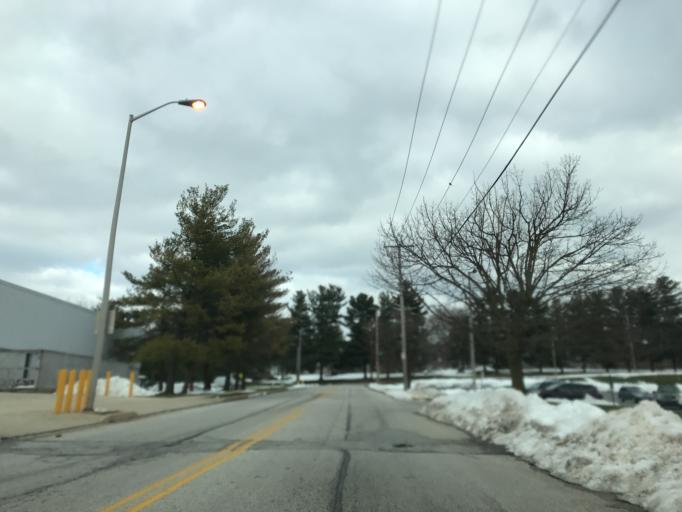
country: US
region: Pennsylvania
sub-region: York County
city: North York
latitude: 39.9851
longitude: -76.7472
